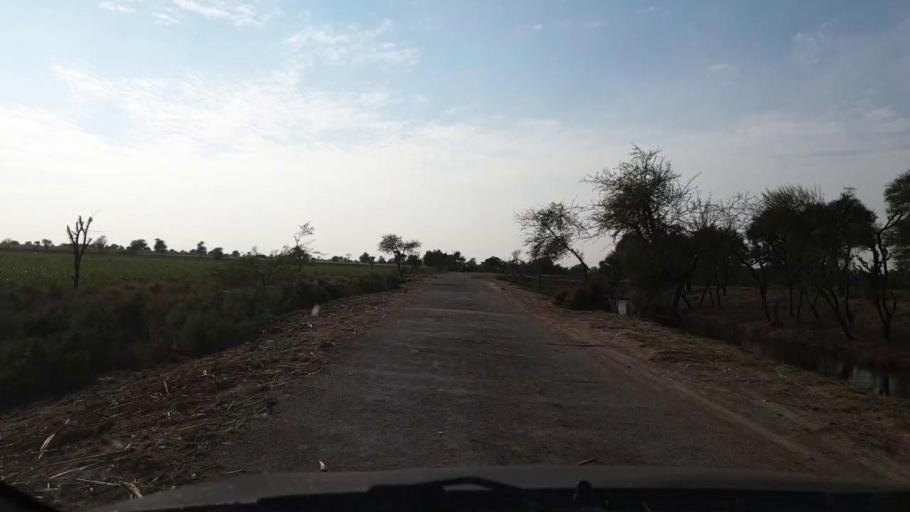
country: PK
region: Sindh
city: Jhol
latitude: 25.9728
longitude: 68.8345
